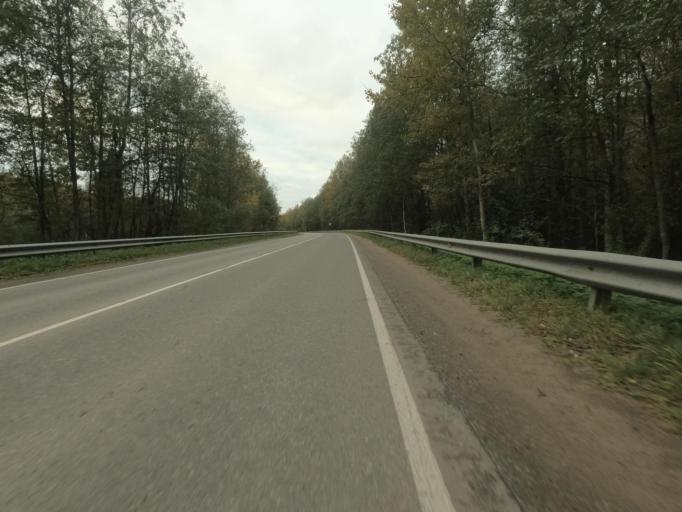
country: RU
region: Leningrad
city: Pavlovo
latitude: 59.7918
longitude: 30.9593
